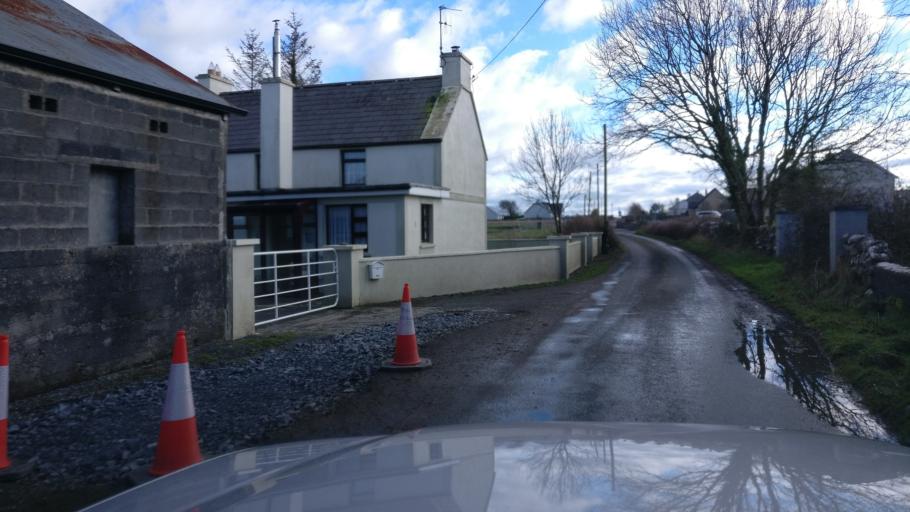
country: IE
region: Connaught
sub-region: County Galway
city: Oranmore
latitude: 53.2799
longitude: -8.8930
